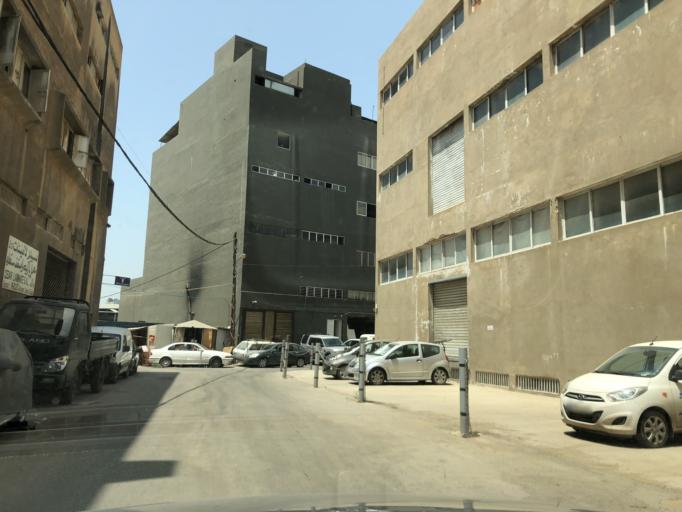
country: LB
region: Mont-Liban
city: Baabda
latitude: 33.8640
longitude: 35.5452
